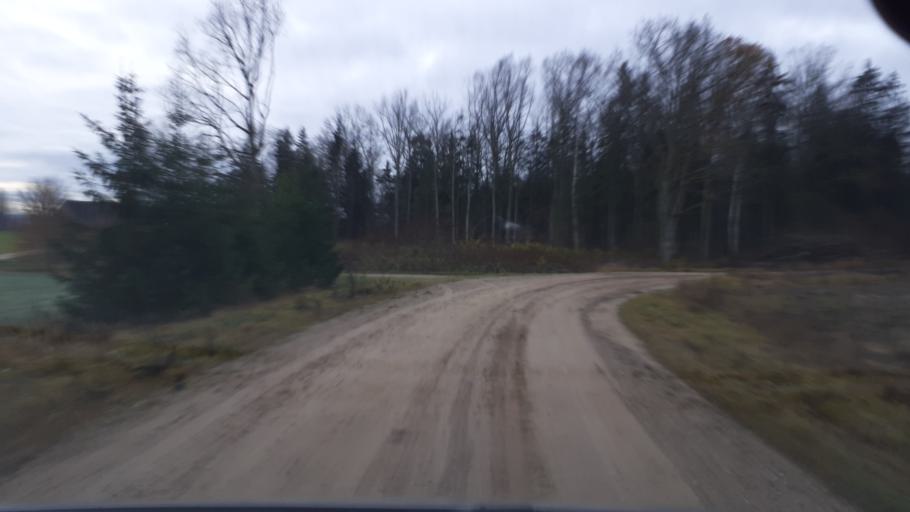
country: LV
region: Kuldigas Rajons
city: Kuldiga
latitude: 57.0001
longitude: 21.9202
